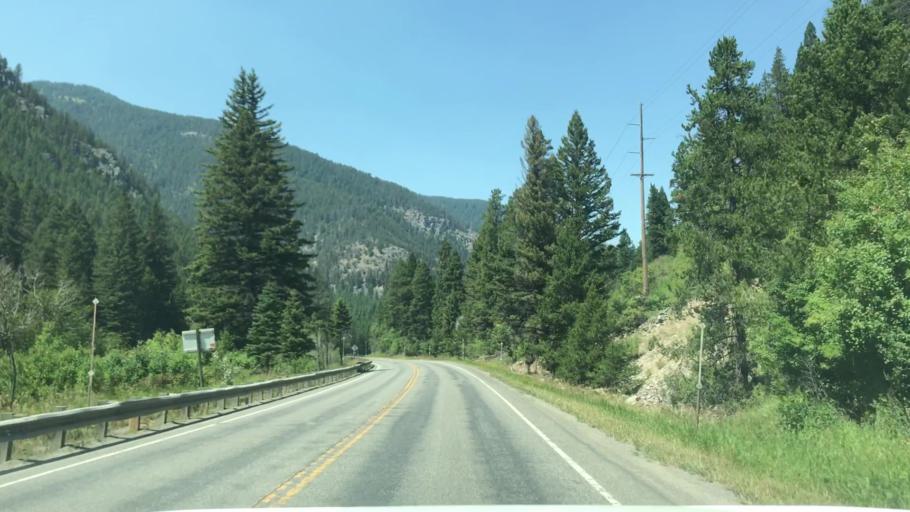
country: US
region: Montana
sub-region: Gallatin County
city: Big Sky
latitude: 45.3970
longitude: -111.2116
